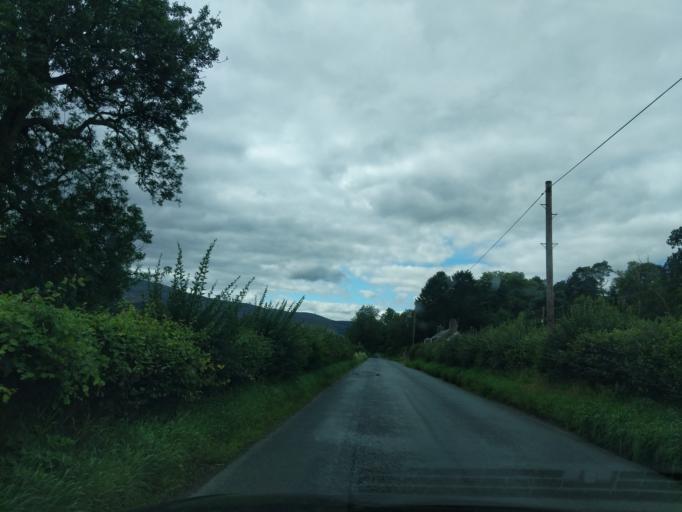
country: GB
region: Scotland
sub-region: The Scottish Borders
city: Peebles
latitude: 55.6243
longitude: -3.2989
